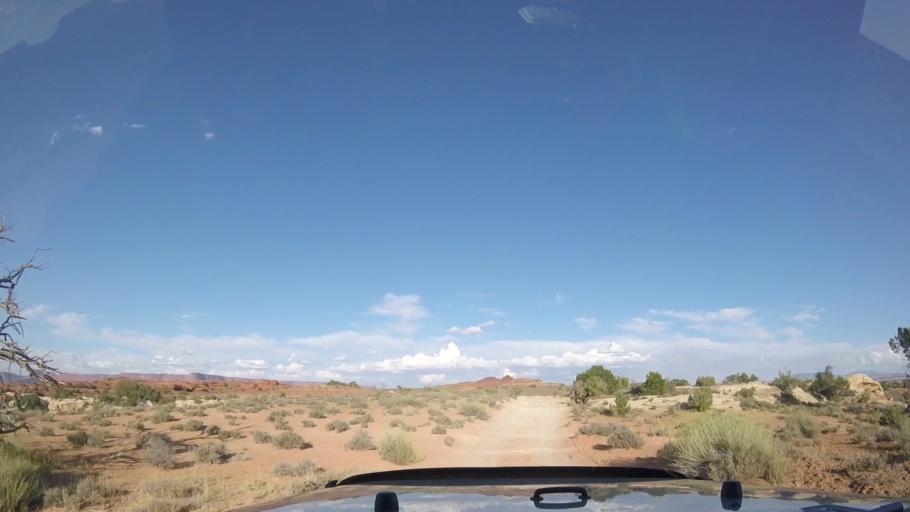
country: US
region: Utah
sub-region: Grand County
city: Moab
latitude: 38.2159
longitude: -109.7974
